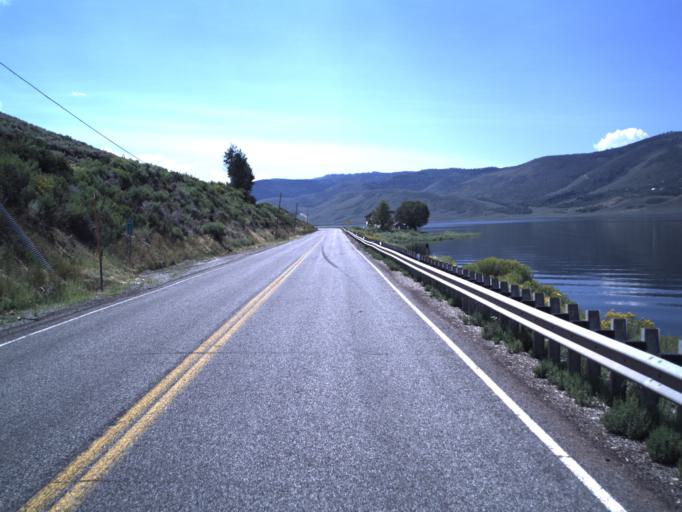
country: US
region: Utah
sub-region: Carbon County
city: Helper
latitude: 39.7793
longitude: -111.1353
